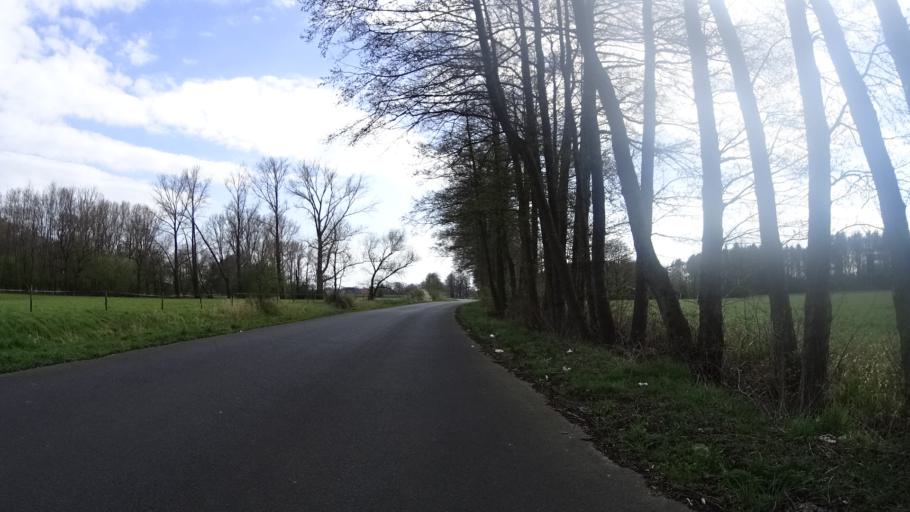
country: DE
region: Lower Saxony
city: Lehe
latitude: 53.0387
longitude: 7.3222
